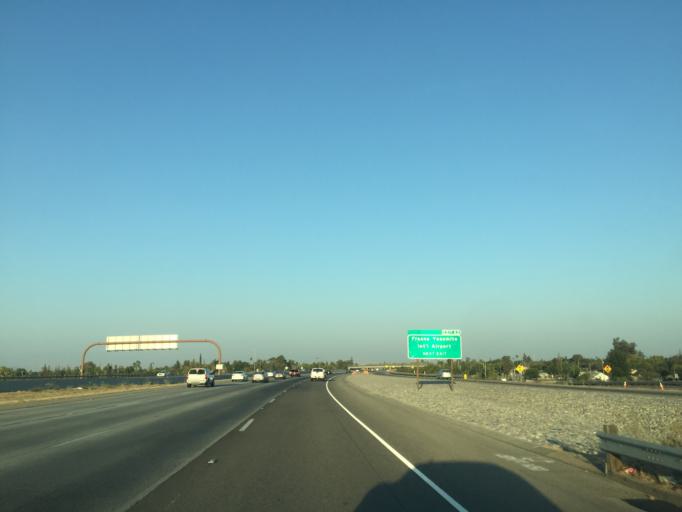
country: US
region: California
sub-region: Fresno County
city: Fresno
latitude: 36.7548
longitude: -119.7403
